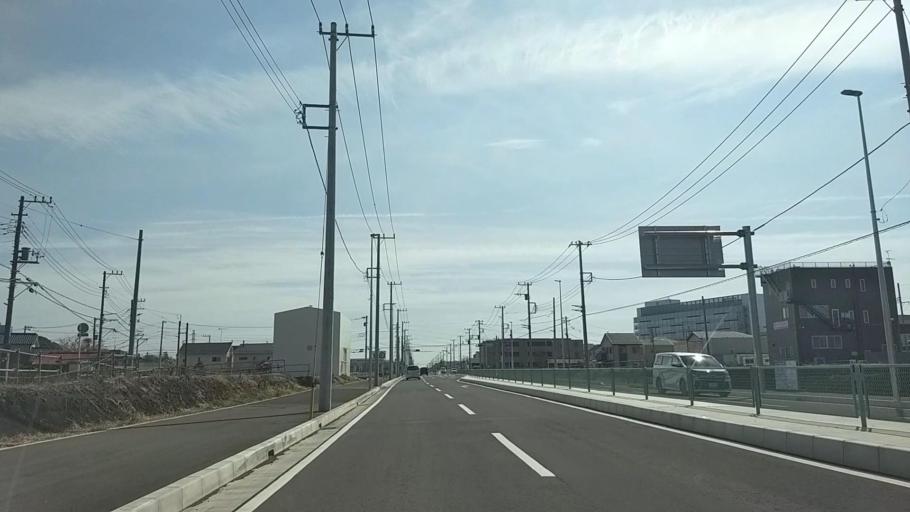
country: JP
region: Kanagawa
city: Fujisawa
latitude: 35.4065
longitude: 139.4539
